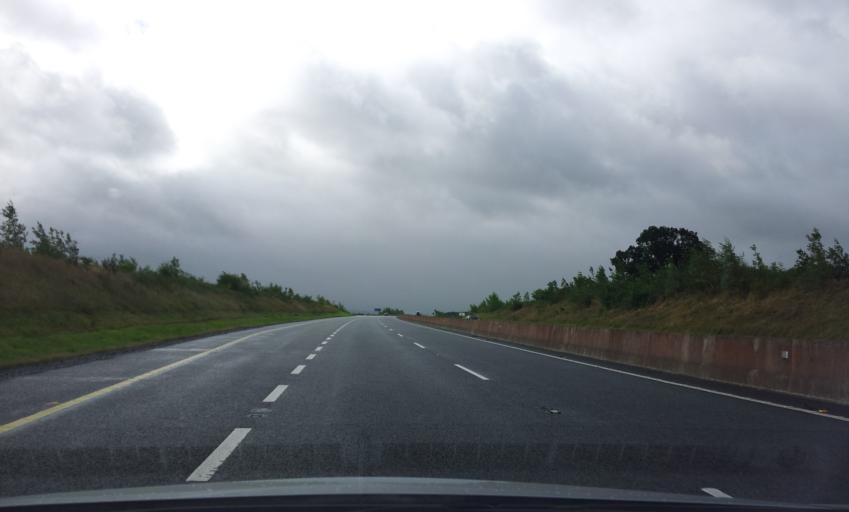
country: IE
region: Leinster
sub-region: Kilkenny
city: Thomastown
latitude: 52.4923
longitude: -7.2417
